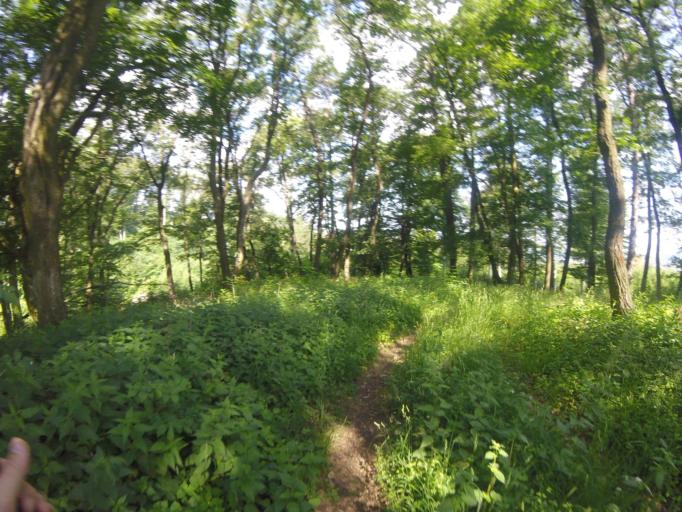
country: HU
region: Fejer
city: Bakonycsernye
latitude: 47.2707
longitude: 18.0411
